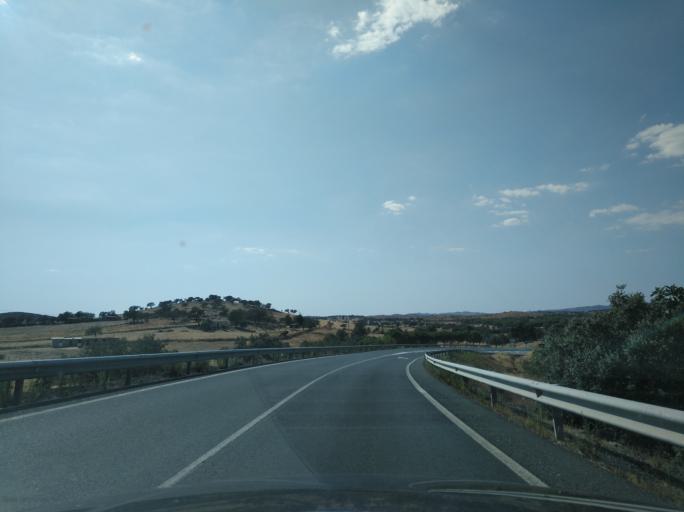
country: ES
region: Andalusia
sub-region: Provincia de Huelva
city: Cabezas Rubias
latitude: 37.7292
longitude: -7.0917
